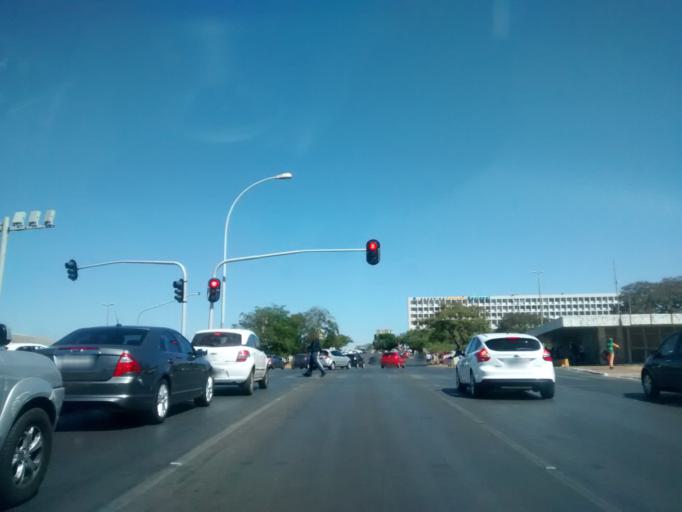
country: BR
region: Federal District
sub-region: Brasilia
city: Brasilia
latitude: -15.7879
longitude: -47.8817
